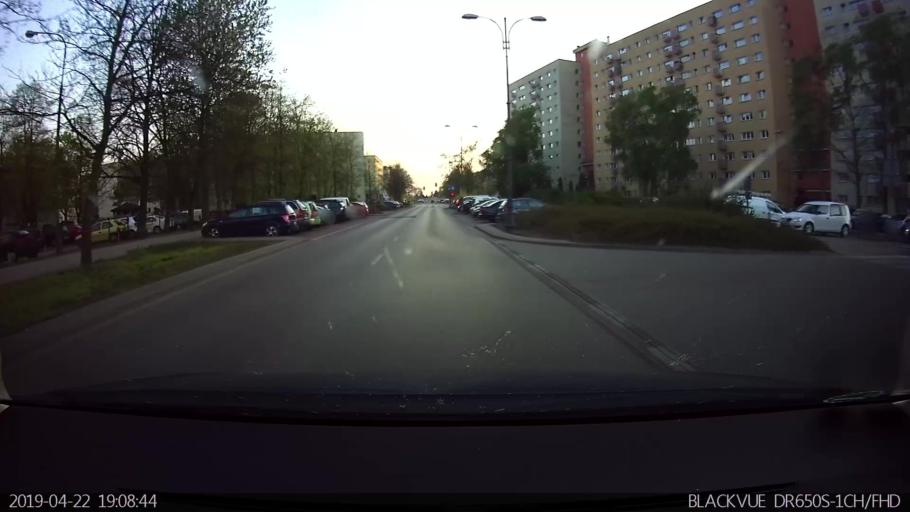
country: PL
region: Masovian Voivodeship
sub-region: Warszawa
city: Bielany
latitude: 52.2705
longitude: 20.9436
